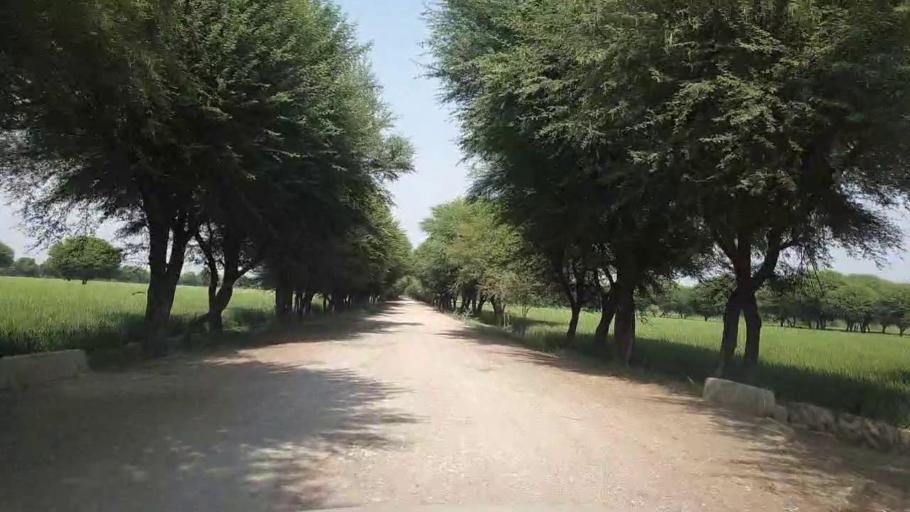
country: PK
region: Sindh
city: Dhoro Naro
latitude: 25.4811
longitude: 69.6212
